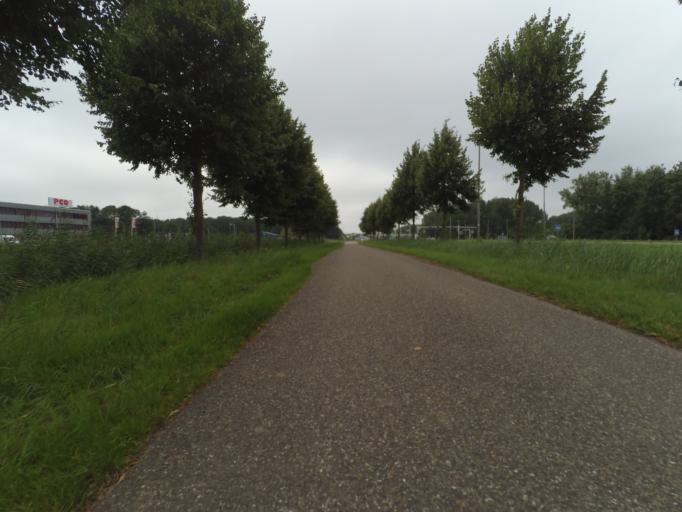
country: NL
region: Flevoland
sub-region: Gemeente Lelystad
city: Lelystad
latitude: 52.4780
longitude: 5.5063
